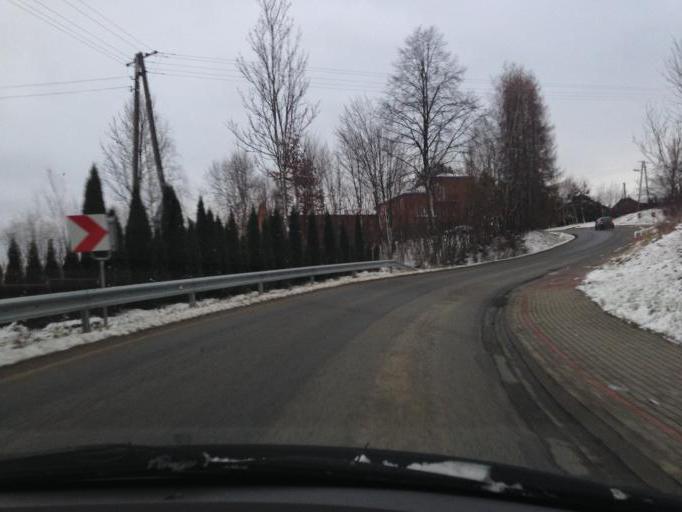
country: PL
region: Lesser Poland Voivodeship
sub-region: Powiat gorlicki
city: Moszczenica
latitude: 49.7300
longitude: 21.0995
